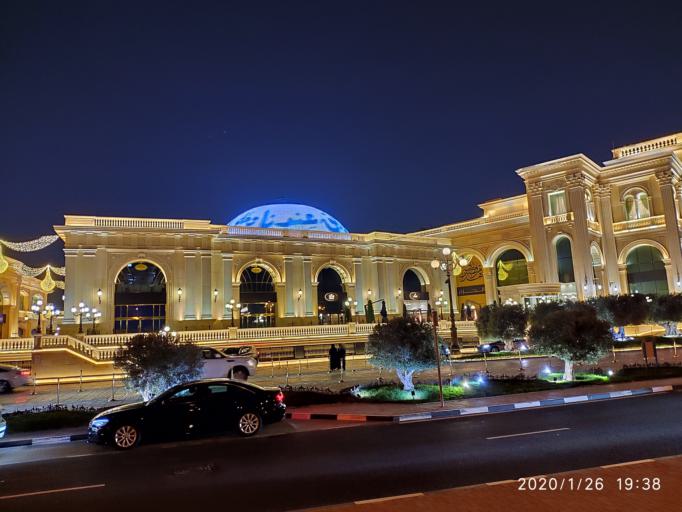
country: QA
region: Baladiyat ad Dawhah
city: Doha
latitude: 25.3332
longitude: 51.4975
